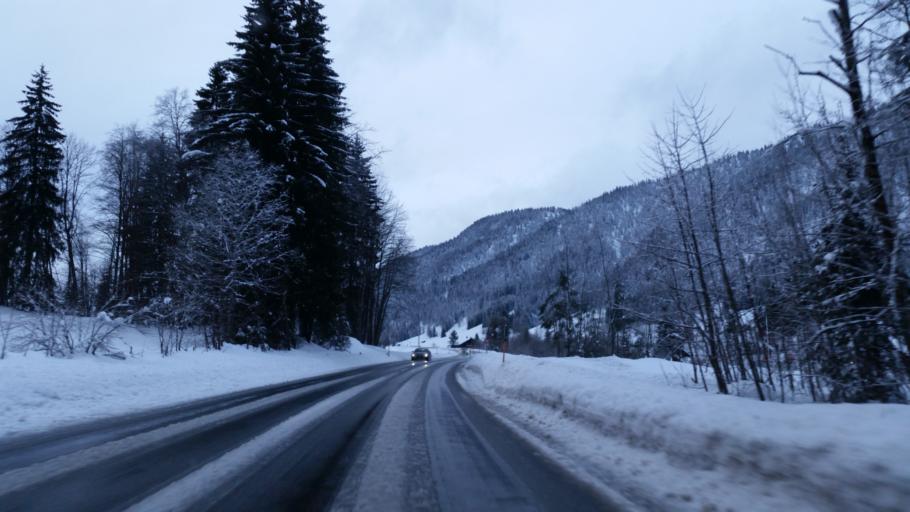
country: AT
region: Tyrol
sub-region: Politischer Bezirk Kitzbuhel
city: Hochfilzen
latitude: 47.4500
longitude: 12.6771
